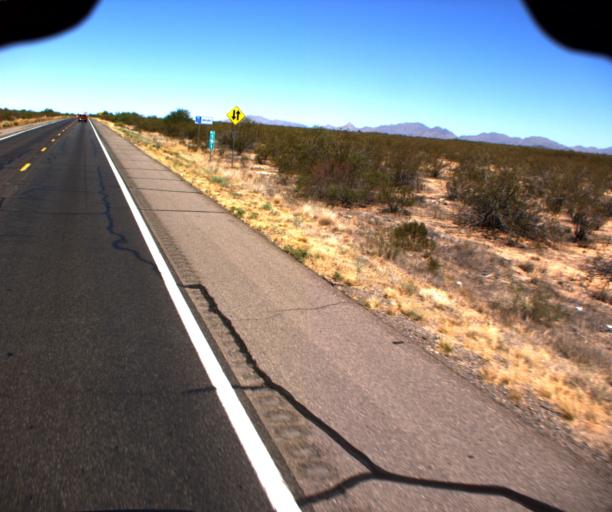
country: US
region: Arizona
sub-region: Yavapai County
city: Congress
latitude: 34.0479
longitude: -112.8420
